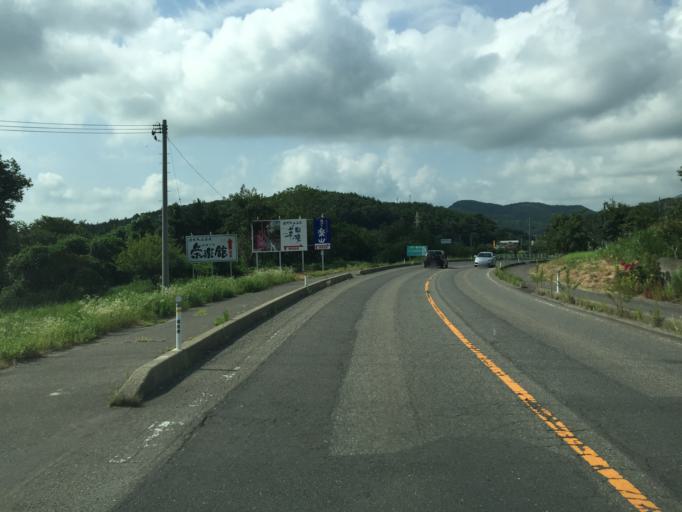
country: JP
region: Fukushima
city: Motomiya
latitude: 37.4915
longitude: 140.2795
